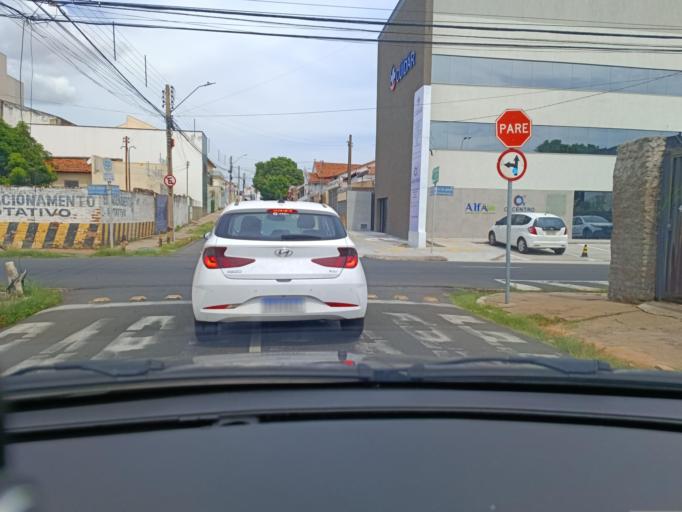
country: BR
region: Piaui
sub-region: Teresina
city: Teresina
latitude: -5.0931
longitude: -42.8104
